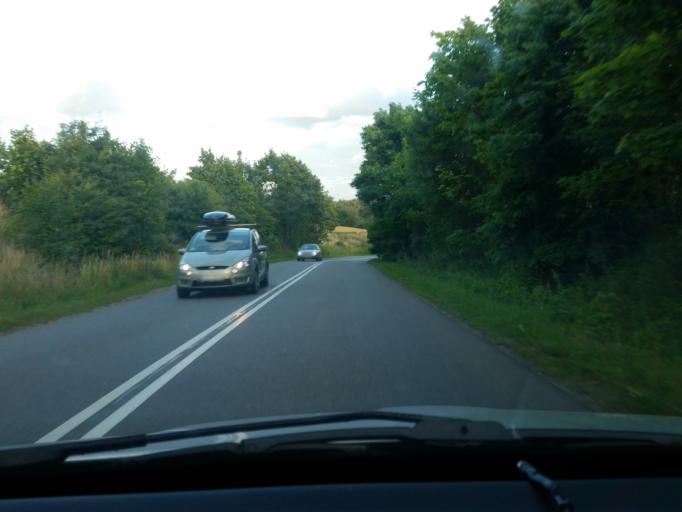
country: PL
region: Pomeranian Voivodeship
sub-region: Powiat czluchowski
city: Przechlewo
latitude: 53.8187
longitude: 17.4076
